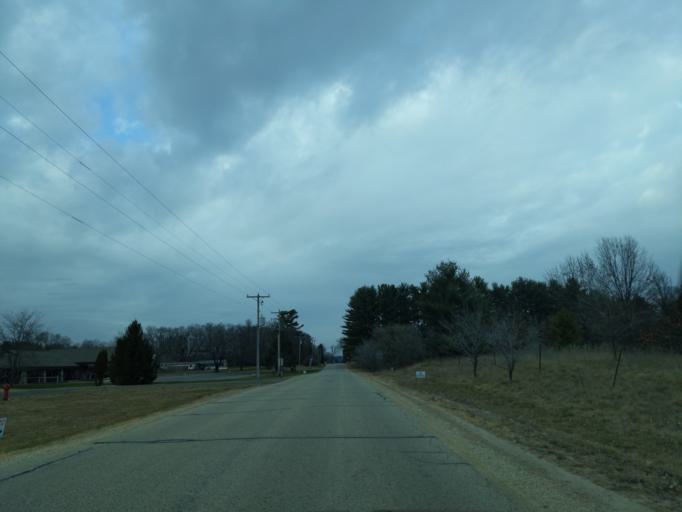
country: US
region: Wisconsin
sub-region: Waushara County
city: Wautoma
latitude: 44.0660
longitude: -89.2773
